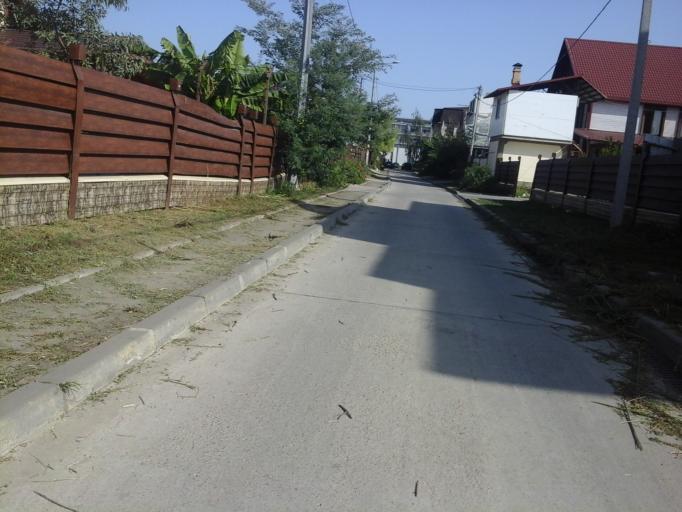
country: RU
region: Krasnodarskiy
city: Adler
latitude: 43.4113
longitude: 39.9632
